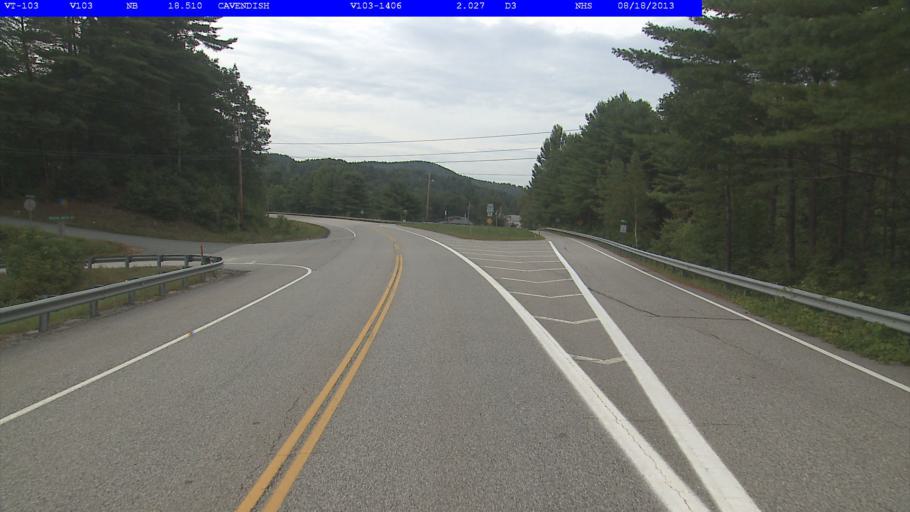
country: US
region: Vermont
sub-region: Windsor County
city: Chester
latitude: 43.3756
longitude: -72.6347
